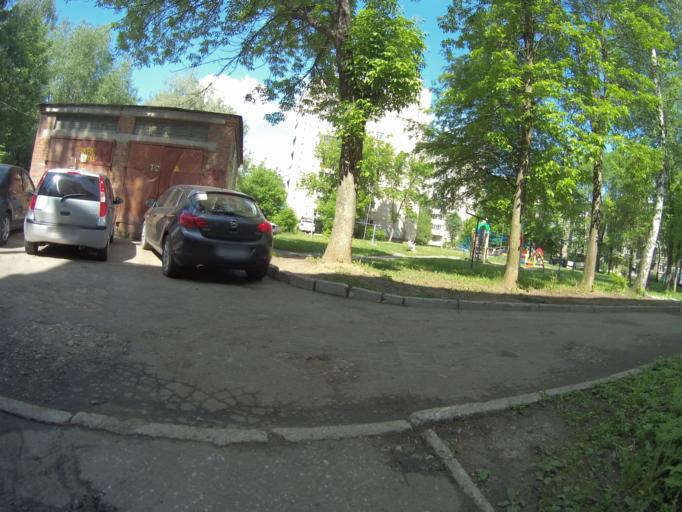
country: RU
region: Vladimir
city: Vladimir
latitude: 56.1302
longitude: 40.3544
